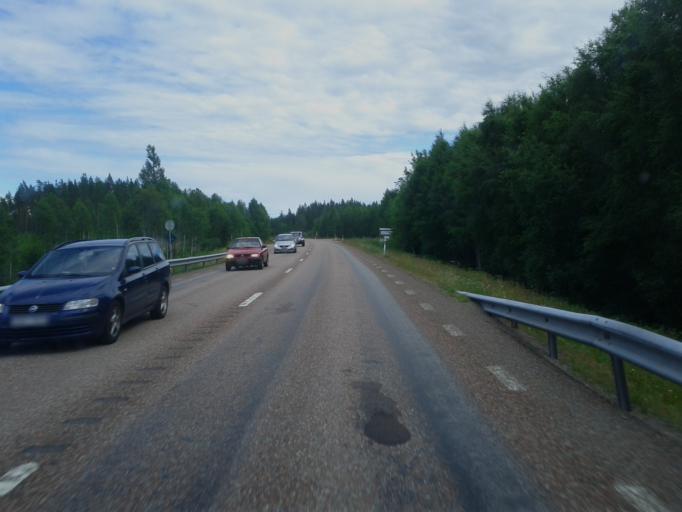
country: SE
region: Dalarna
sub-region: Faluns Kommun
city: Bjursas
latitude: 60.7867
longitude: 15.2881
